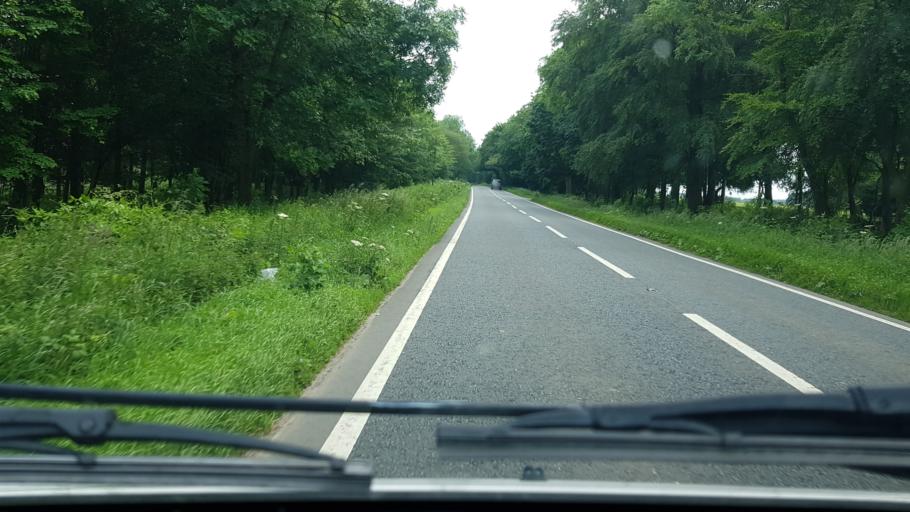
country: GB
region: England
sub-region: Worcestershire
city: Broadway
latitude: 52.0255
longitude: -1.8185
